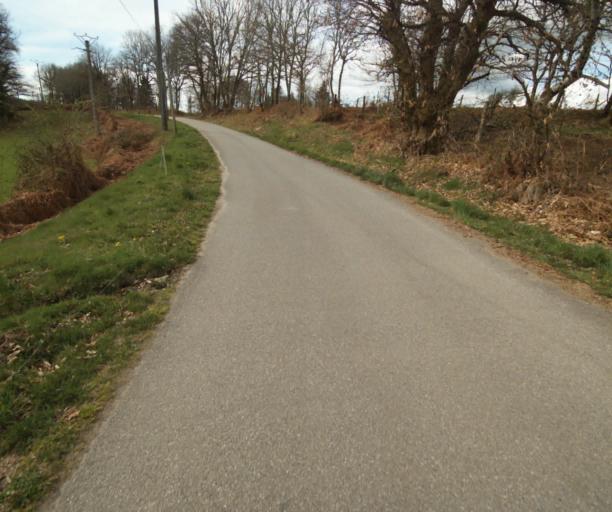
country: FR
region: Limousin
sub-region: Departement de la Correze
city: Correze
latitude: 45.3911
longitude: 1.8982
